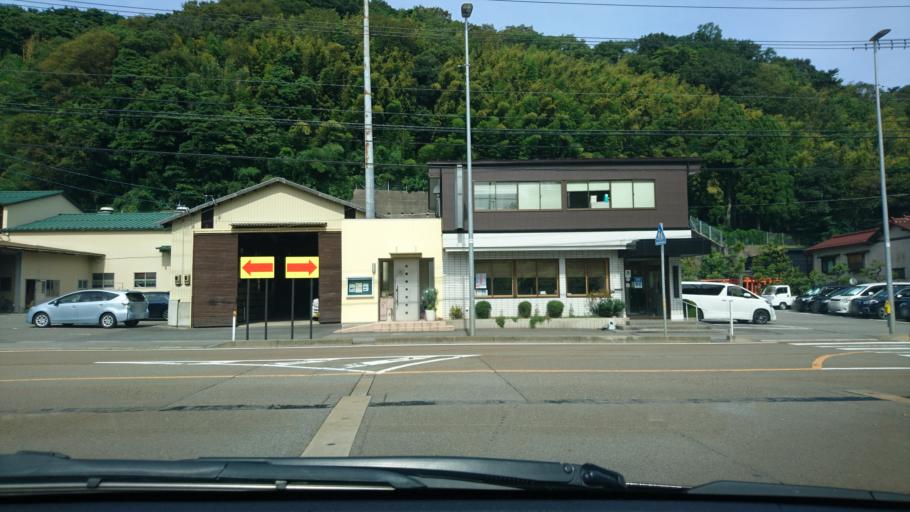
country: JP
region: Fukui
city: Maruoka
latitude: 36.3041
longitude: 136.3025
